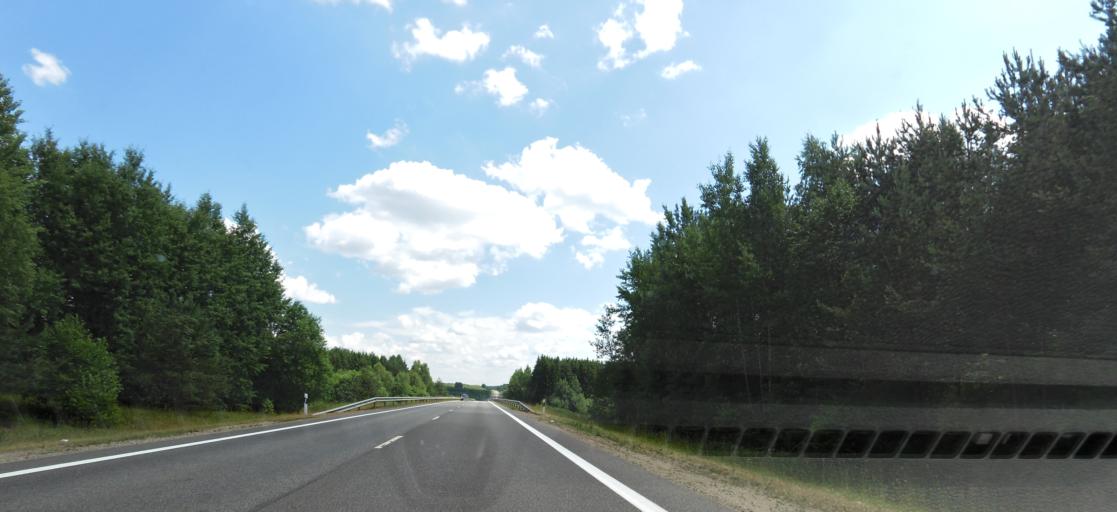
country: LT
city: Skaidiskes
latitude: 54.5842
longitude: 25.5819
